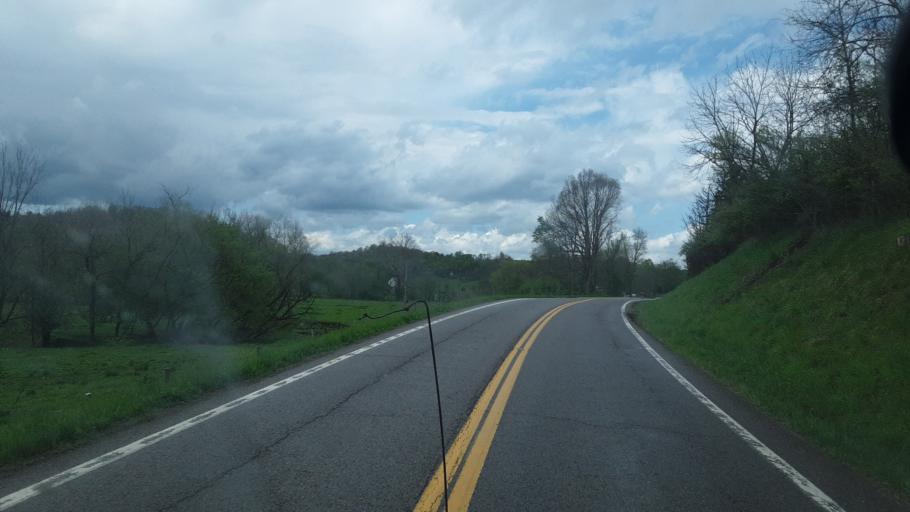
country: US
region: Ohio
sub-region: Guernsey County
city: Mantua
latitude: 40.1061
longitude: -81.7666
